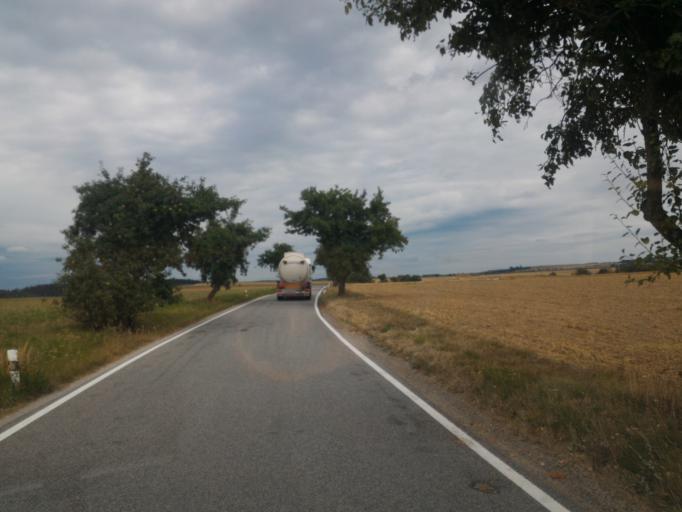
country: CZ
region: Vysocina
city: Zeletava
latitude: 49.1581
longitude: 15.5801
